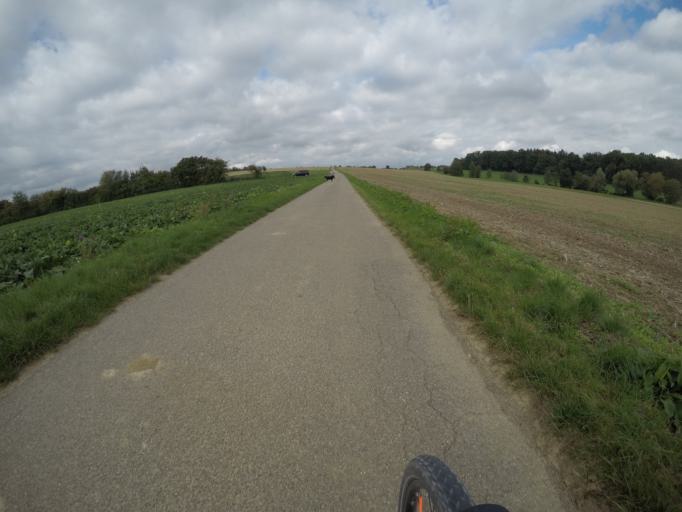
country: DE
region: Baden-Wuerttemberg
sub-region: Regierungsbezirk Stuttgart
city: Renningen
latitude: 48.7426
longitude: 8.9164
